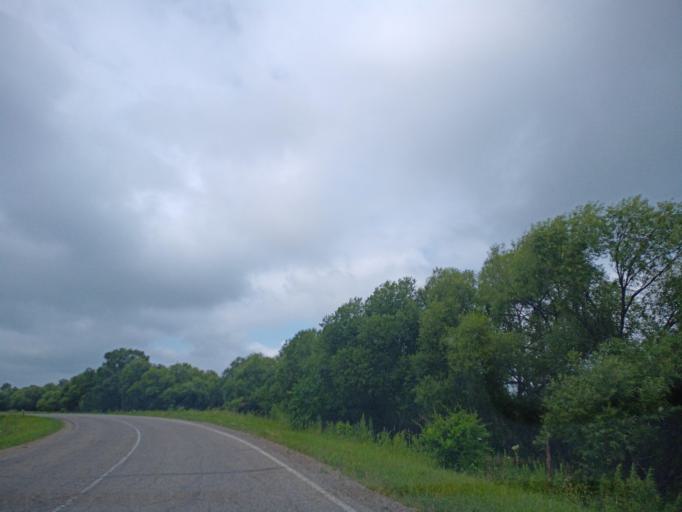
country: RU
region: Primorskiy
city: Dal'nerechensk
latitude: 45.9463
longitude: 133.8873
